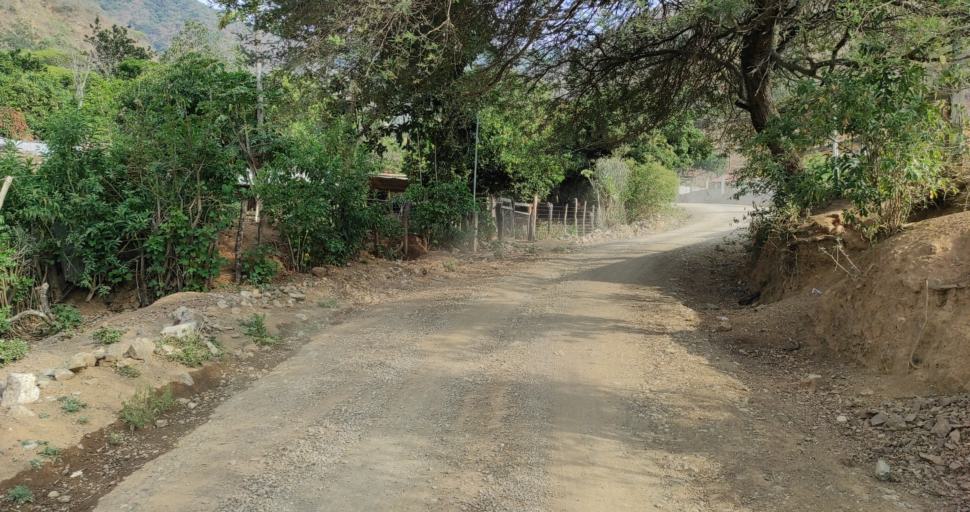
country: EC
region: Loja
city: Catacocha
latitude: -3.9925
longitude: -79.6982
